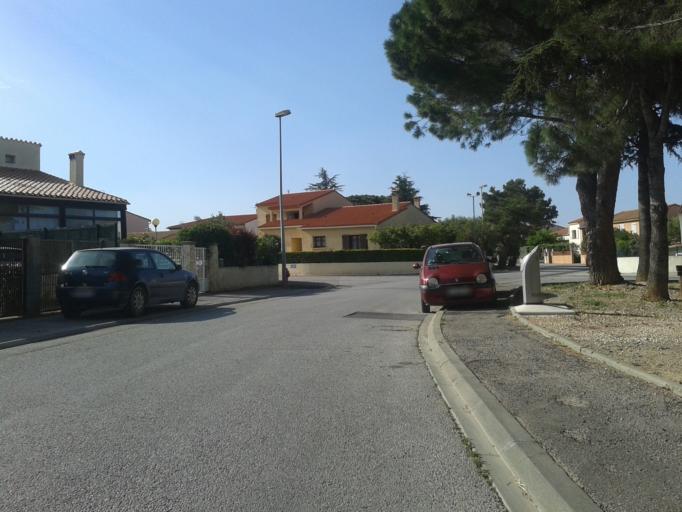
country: FR
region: Languedoc-Roussillon
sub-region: Departement des Pyrenees-Orientales
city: Pezilla-la-Riviere
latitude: 42.6950
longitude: 2.7771
